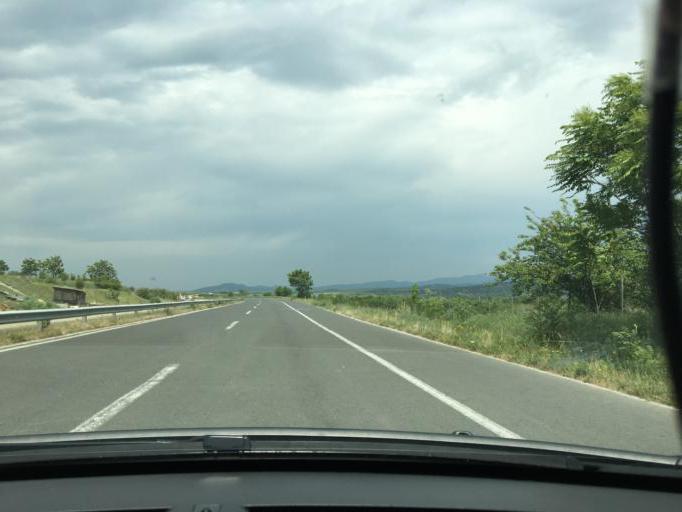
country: MK
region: Demir Kapija
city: Demir Kapija
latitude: 41.4437
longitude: 22.1799
